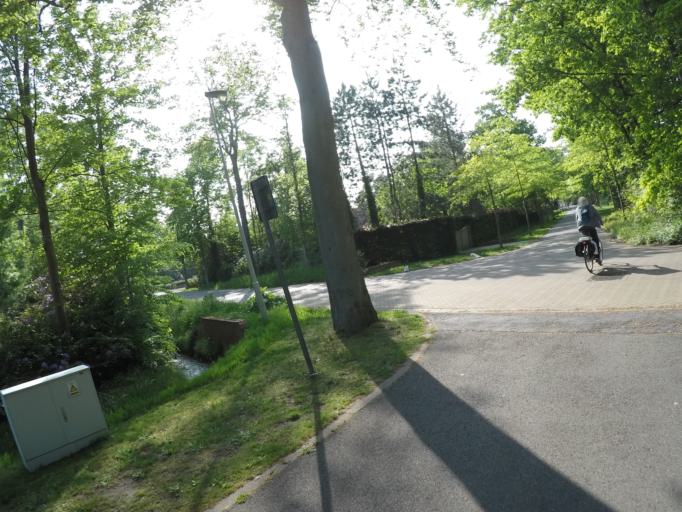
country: BE
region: Flanders
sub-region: Provincie Antwerpen
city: Schoten
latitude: 51.2579
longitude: 4.5349
